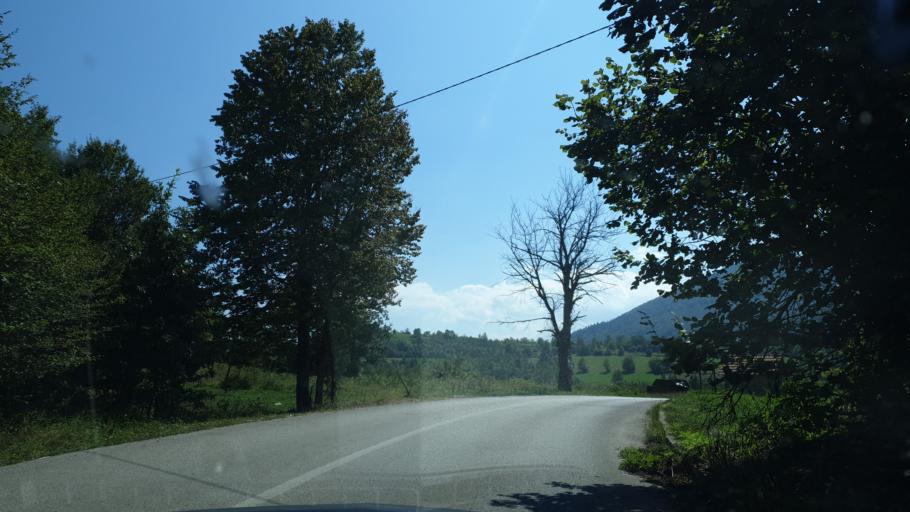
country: RS
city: Zlatibor
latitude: 43.6575
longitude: 19.8330
